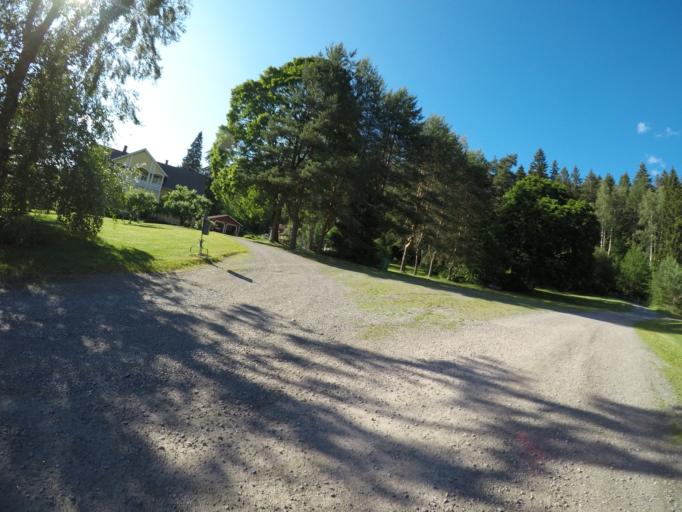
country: FI
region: Haeme
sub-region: Haemeenlinna
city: Haemeenlinna
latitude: 61.0230
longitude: 24.4992
